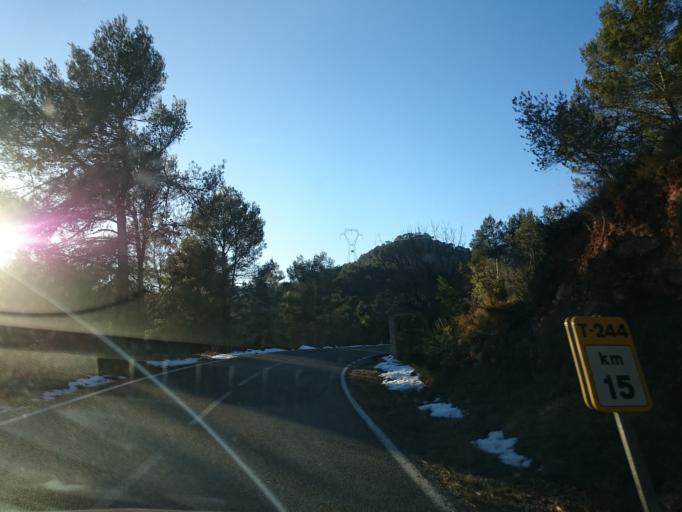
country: ES
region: Catalonia
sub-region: Provincia de Tarragona
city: la Bisbal del Penedes
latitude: 41.3758
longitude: 1.4811
